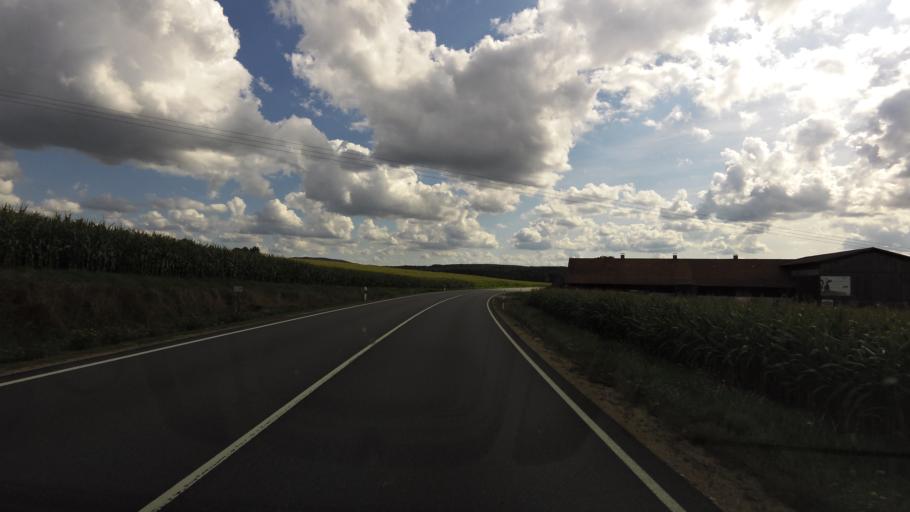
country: DE
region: Bavaria
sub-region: Upper Palatinate
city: Cham
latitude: 49.1925
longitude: 12.6563
